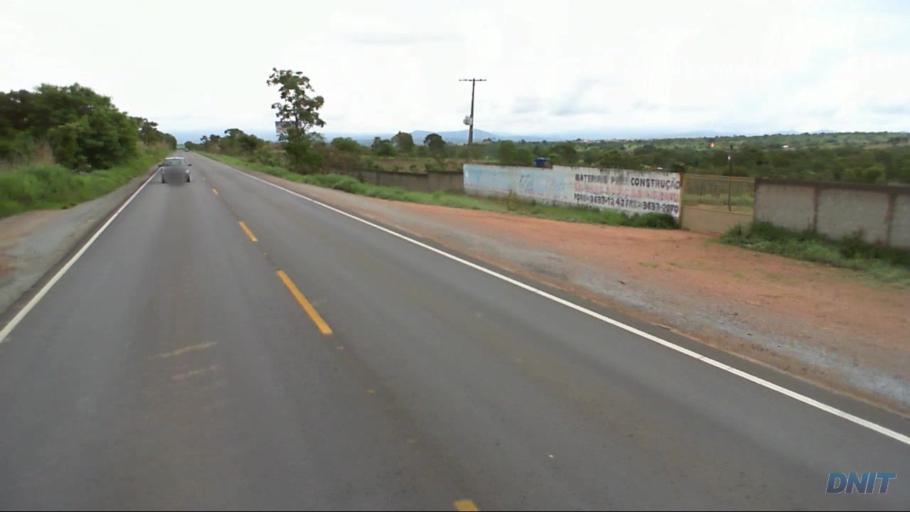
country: BR
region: Goias
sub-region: Padre Bernardo
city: Padre Bernardo
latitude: -15.1938
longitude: -48.2841
